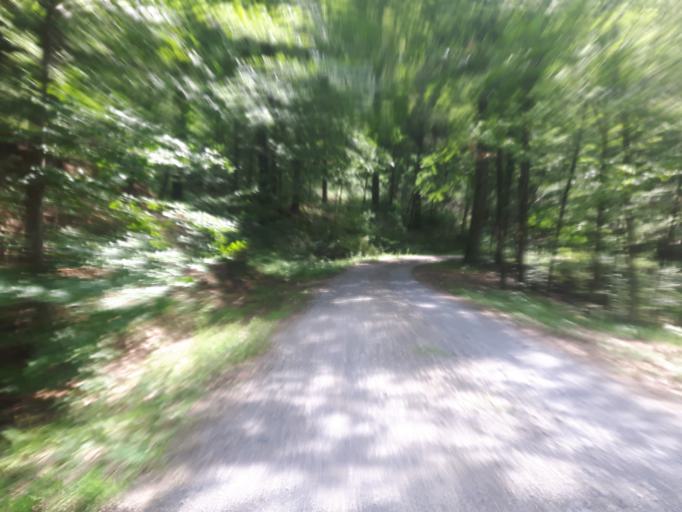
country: DE
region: Baden-Wuerttemberg
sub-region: Regierungsbezirk Stuttgart
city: Pfaffenhofen
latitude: 49.0432
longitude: 8.9552
